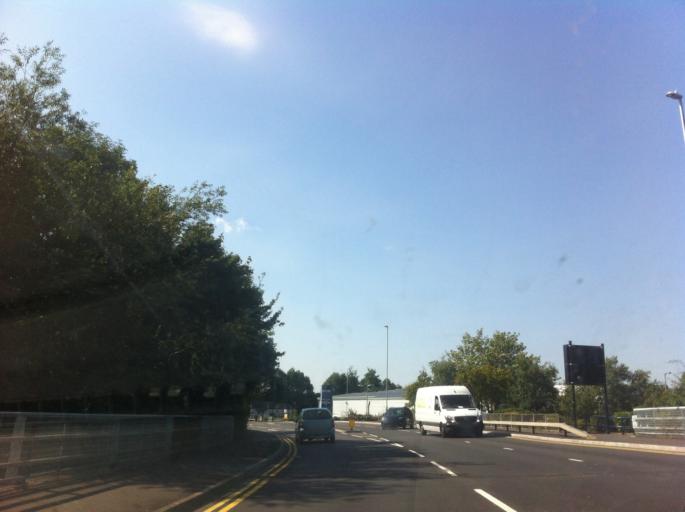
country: GB
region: England
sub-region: Northamptonshire
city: Northampton
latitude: 52.2343
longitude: -0.9001
